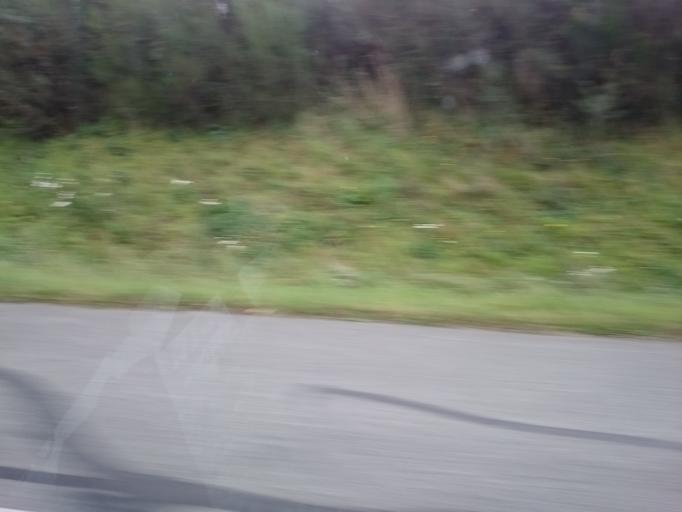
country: FR
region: Brittany
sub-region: Departement des Cotes-d'Armor
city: Plenee-Jugon
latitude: 48.3795
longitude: -2.3702
